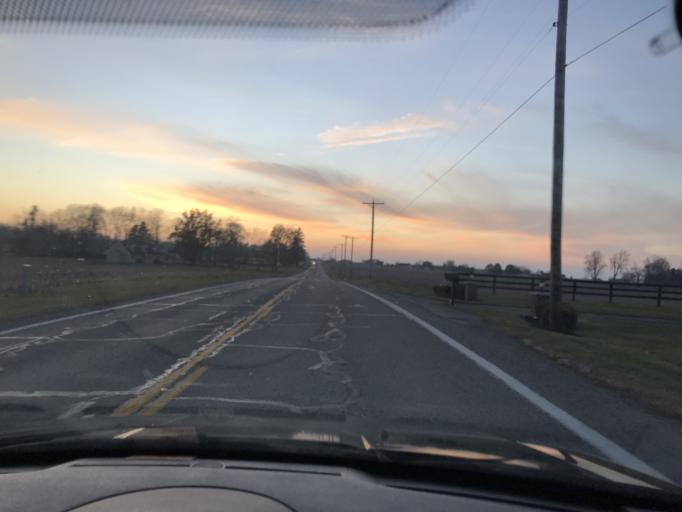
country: US
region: Ohio
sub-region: Champaign County
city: Urbana
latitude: 40.1085
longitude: -83.7030
